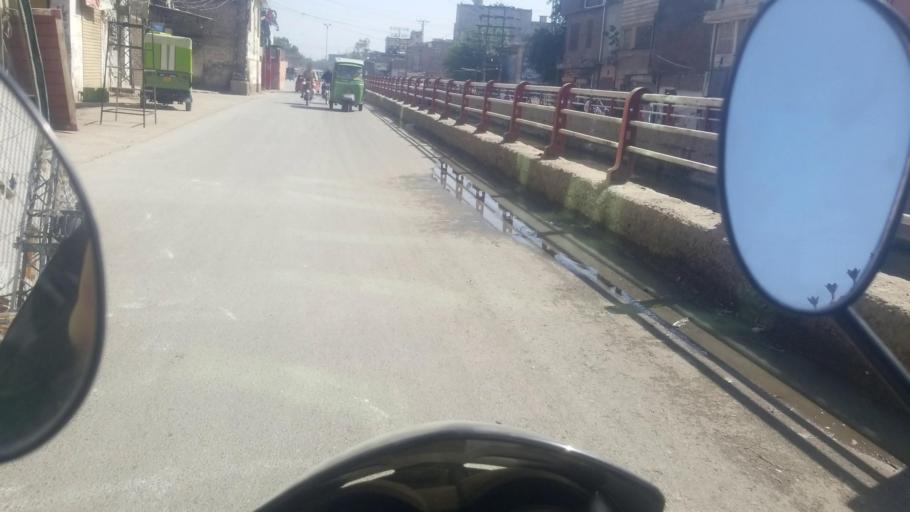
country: PK
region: Khyber Pakhtunkhwa
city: Peshawar
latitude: 34.0200
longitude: 71.5926
